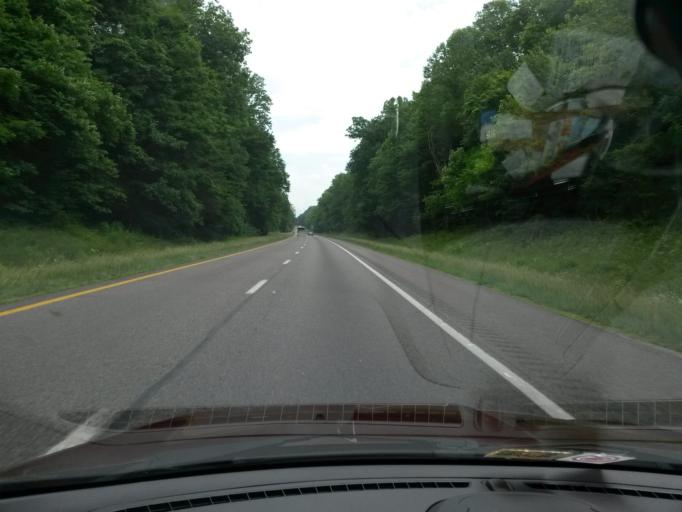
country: US
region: Virginia
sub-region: Goochland County
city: Goochland
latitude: 37.7172
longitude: -77.8075
